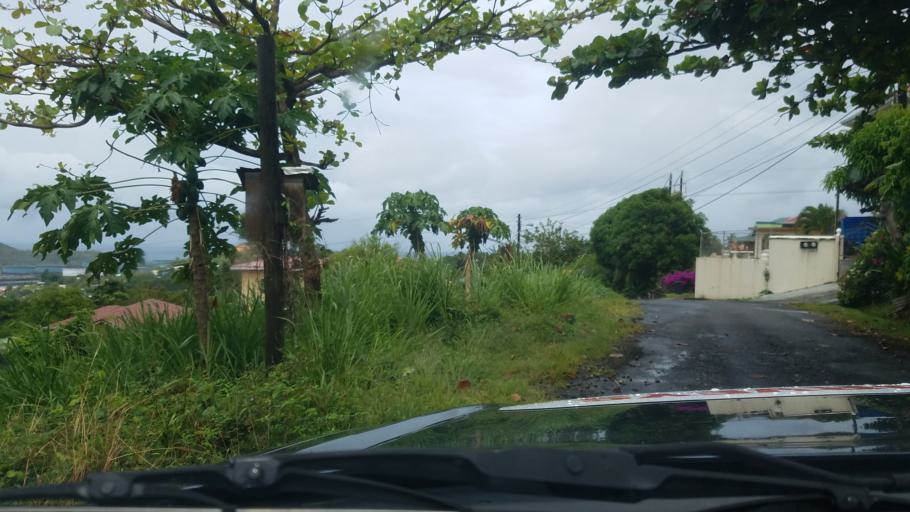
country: LC
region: Castries Quarter
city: Castries
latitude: 13.9946
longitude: -61.0001
